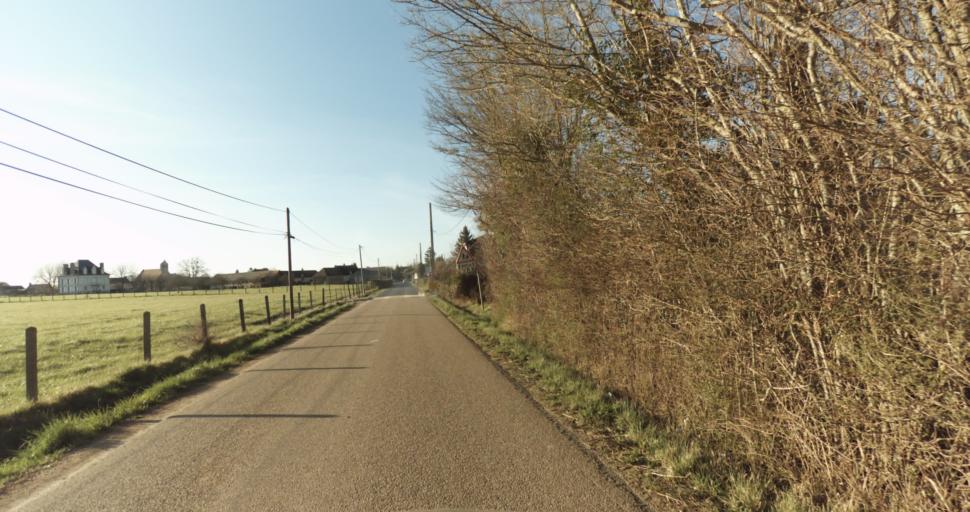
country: FR
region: Lower Normandy
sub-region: Departement du Calvados
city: Saint-Pierre-sur-Dives
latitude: 48.9879
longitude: -0.0165
